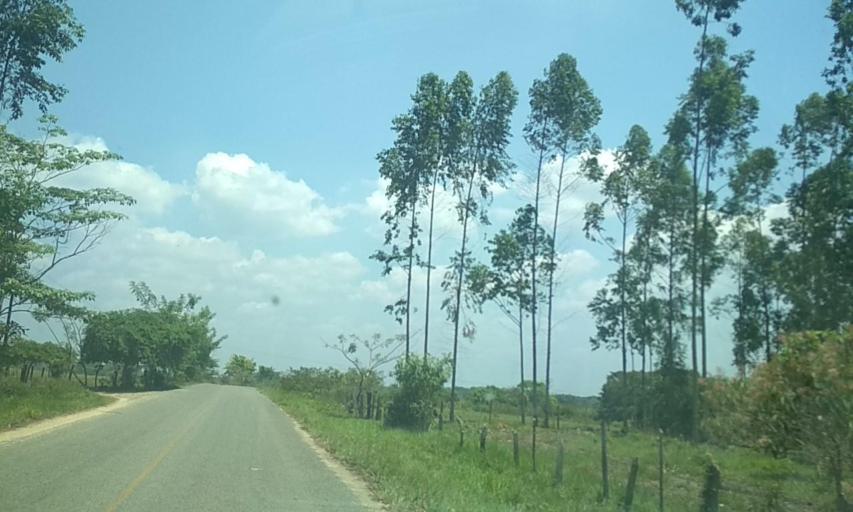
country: MX
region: Tabasco
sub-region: Huimanguillo
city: Francisco Rueda
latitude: 17.8315
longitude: -93.8737
